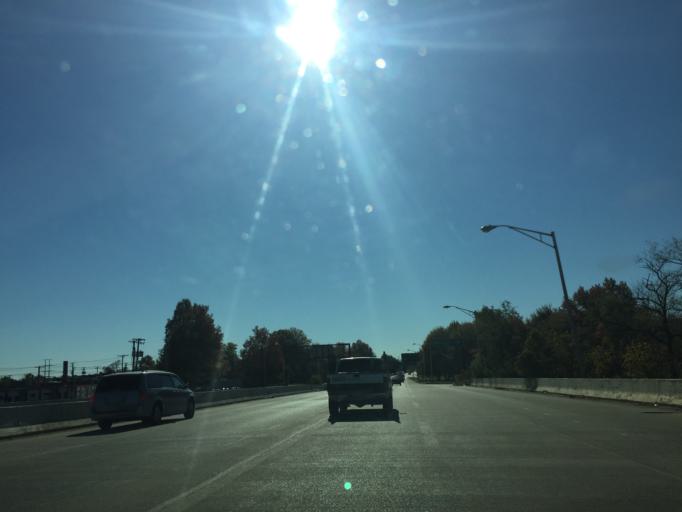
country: US
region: Maryland
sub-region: Baltimore County
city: Lansdowne
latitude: 39.2656
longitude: -76.6354
